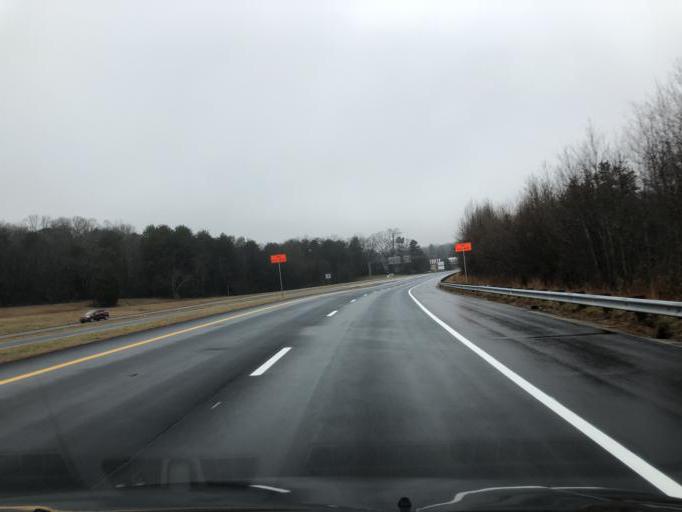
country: US
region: North Carolina
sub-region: Rutherford County
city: Forest City
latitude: 35.3142
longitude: -81.8758
